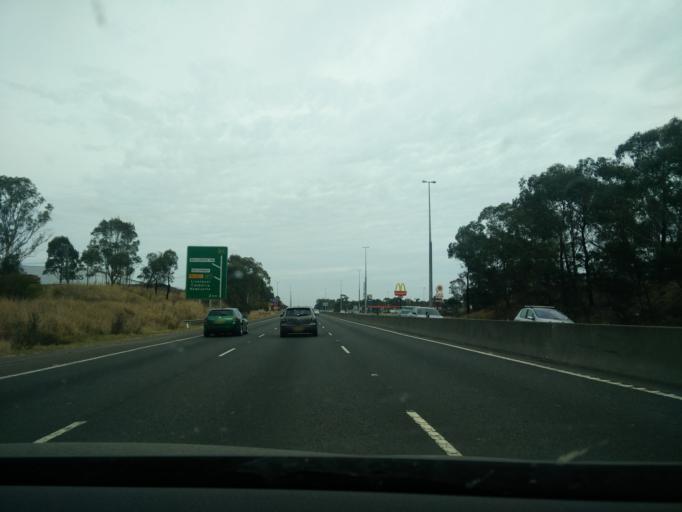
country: AU
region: New South Wales
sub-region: Blacktown
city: Doonside
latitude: -33.8024
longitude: 150.8900
